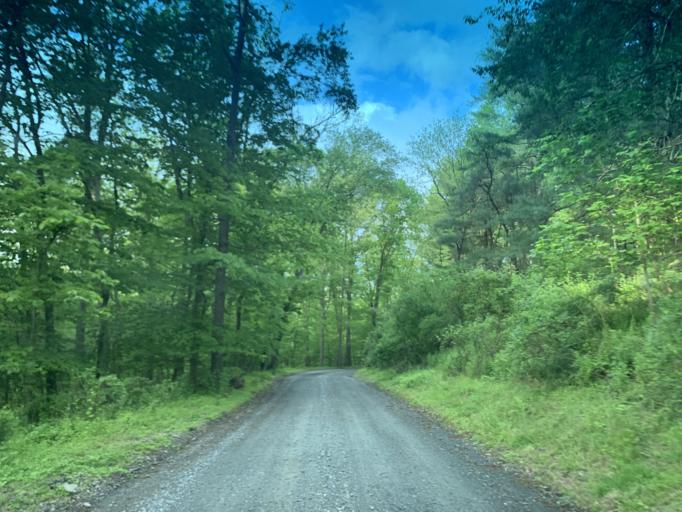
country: US
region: Pennsylvania
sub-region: York County
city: Susquehanna Trails
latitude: 39.6982
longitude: -76.2701
